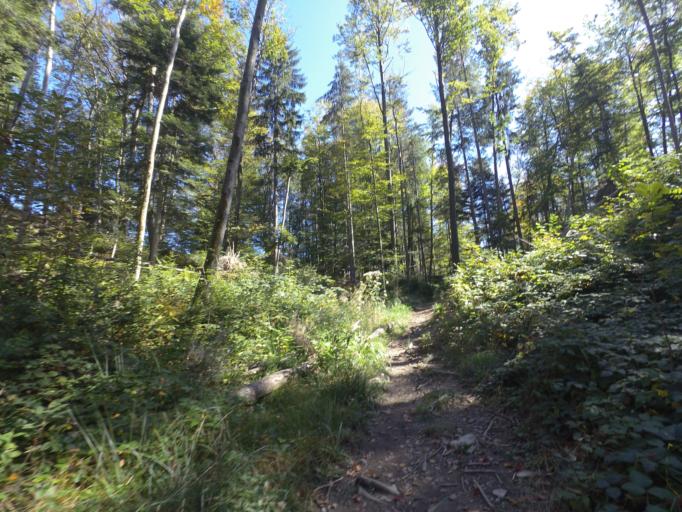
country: AT
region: Salzburg
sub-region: Politischer Bezirk Hallein
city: Hallein
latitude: 47.6864
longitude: 13.0810
